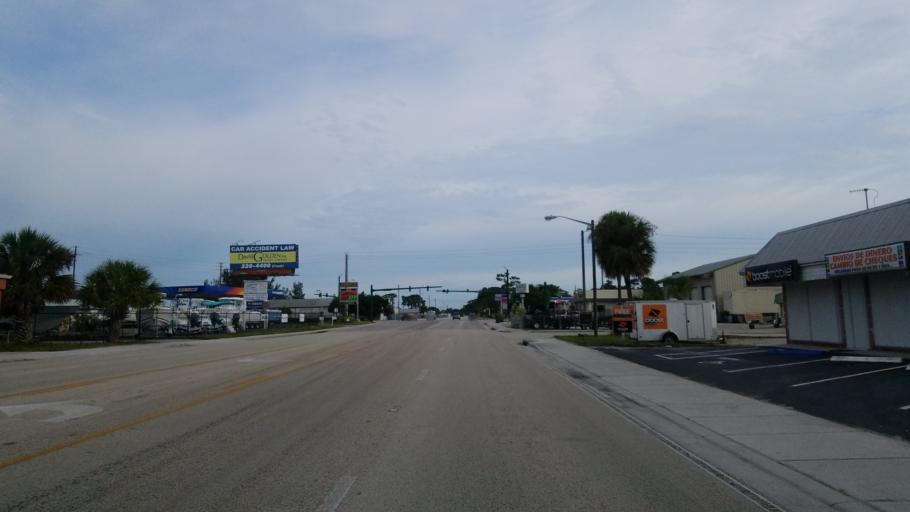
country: US
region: Florida
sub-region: Martin County
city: Port Salerno
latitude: 27.1670
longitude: -80.2208
